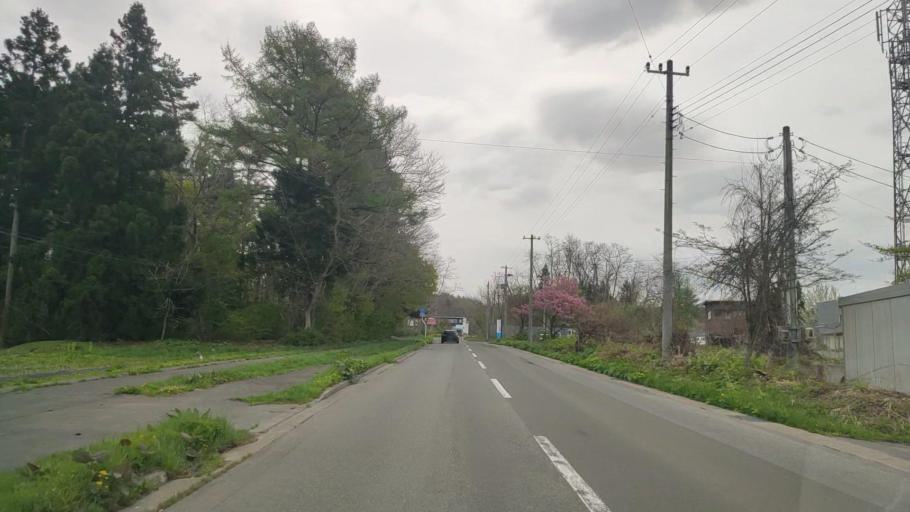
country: JP
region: Aomori
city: Aomori Shi
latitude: 40.7683
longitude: 140.8004
